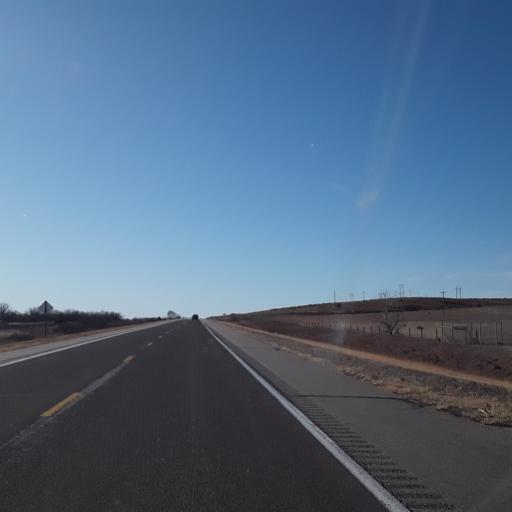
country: US
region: Nebraska
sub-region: Hitchcock County
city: Trenton
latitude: 40.1582
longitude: -101.1732
